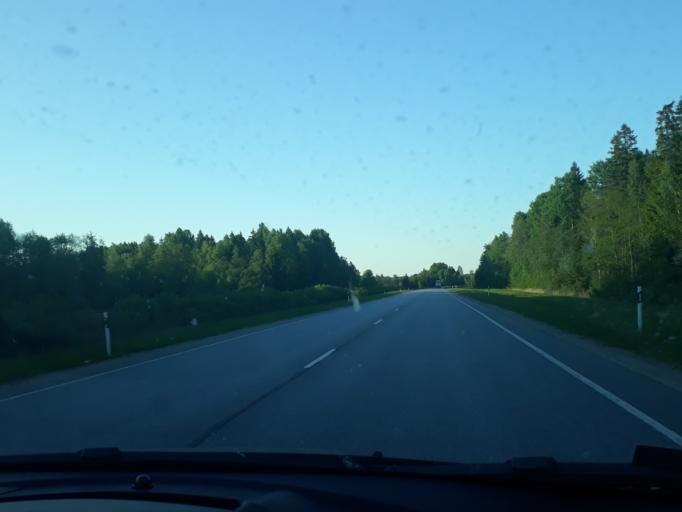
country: EE
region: Paernumaa
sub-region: Sindi linn
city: Sindi
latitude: 58.4574
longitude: 24.6972
